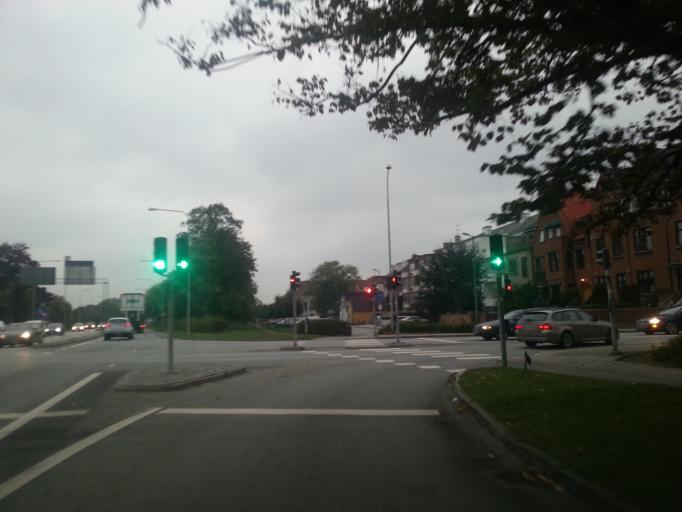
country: SE
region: Skane
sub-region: Trelleborgs Kommun
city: Trelleborg
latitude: 55.3740
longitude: 13.1471
